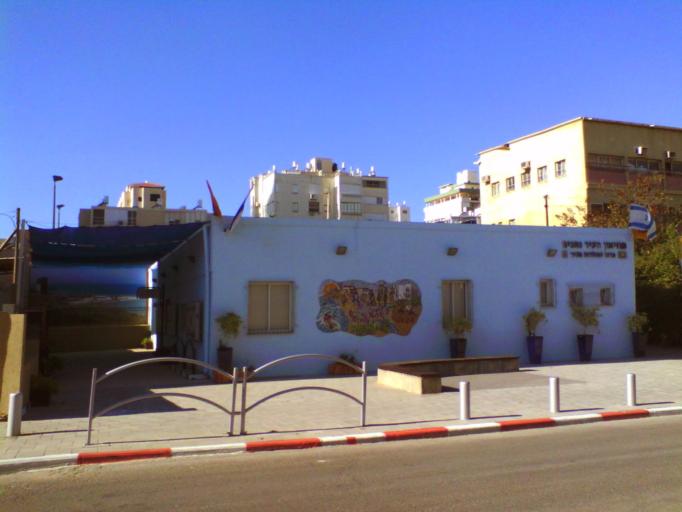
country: IL
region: Central District
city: Netanya
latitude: 32.3325
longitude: 34.8528
